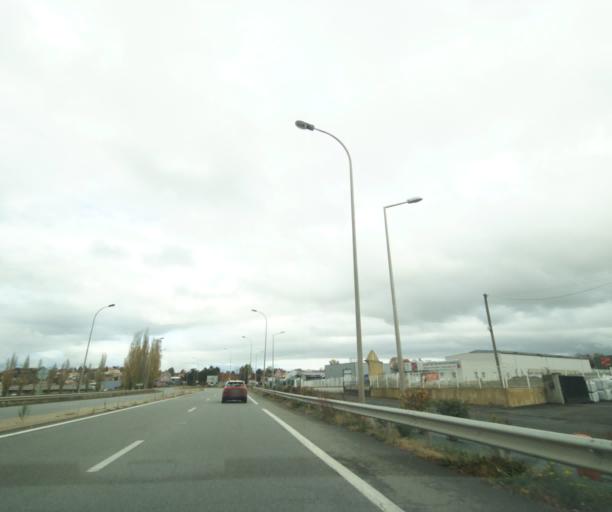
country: FR
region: Auvergne
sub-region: Departement du Puy-de-Dome
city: Dallet
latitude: 45.7911
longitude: 3.2259
